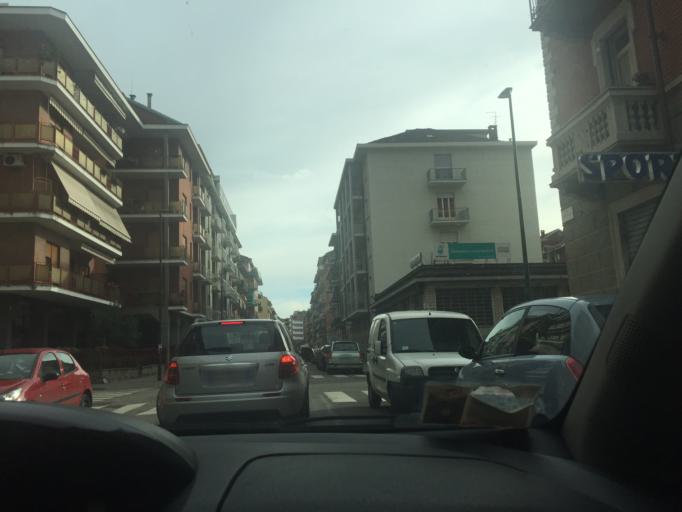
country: IT
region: Piedmont
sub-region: Provincia di Torino
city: Lesna
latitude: 45.0675
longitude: 7.6413
